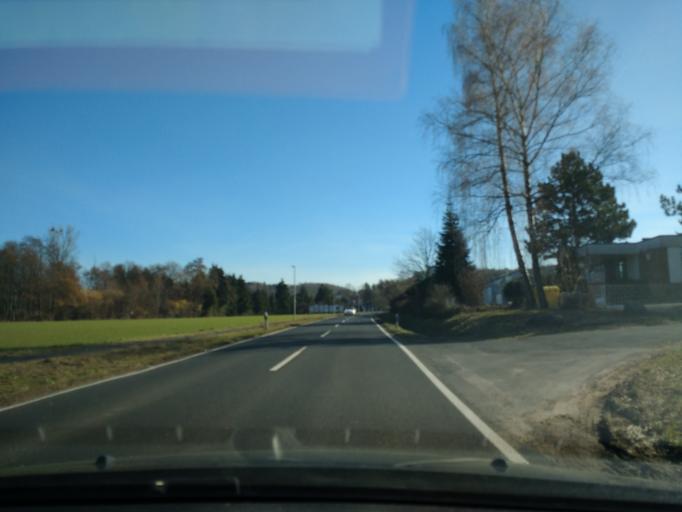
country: DE
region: Bavaria
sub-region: Regierungsbezirk Unterfranken
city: Geiselbach
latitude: 50.1378
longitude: 9.1515
